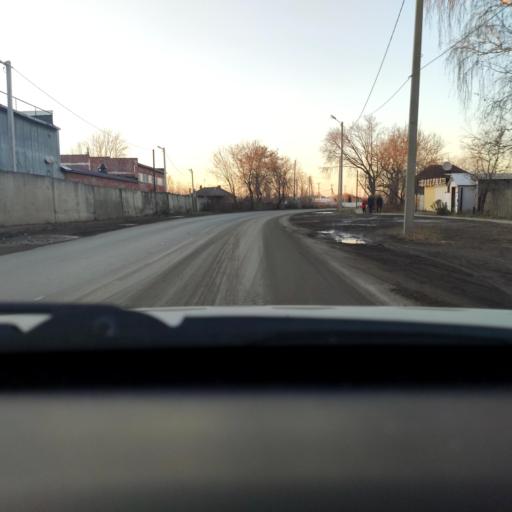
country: RU
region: Perm
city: Kondratovo
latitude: 57.9494
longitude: 56.1400
